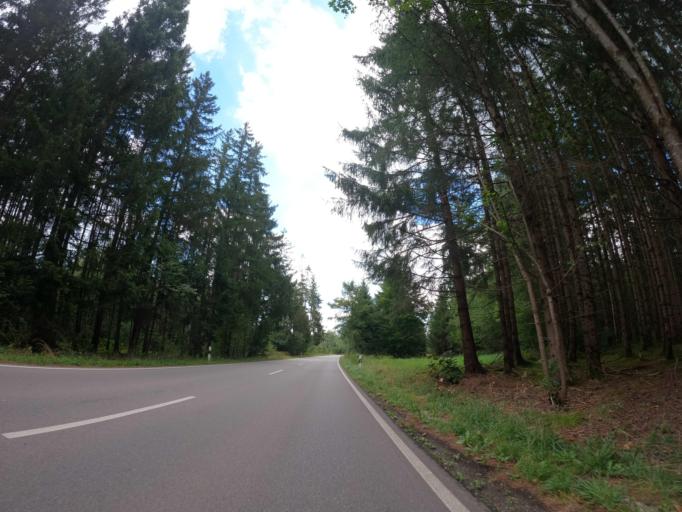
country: DE
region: Bavaria
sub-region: Upper Bavaria
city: Ottobrunn
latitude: 48.0404
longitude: 11.6720
